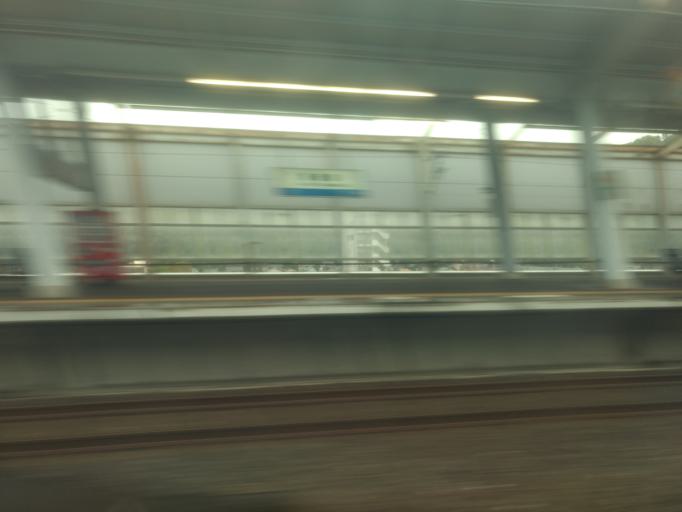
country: JP
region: Yamaguchi
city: Iwakuni
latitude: 34.1649
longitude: 132.1499
